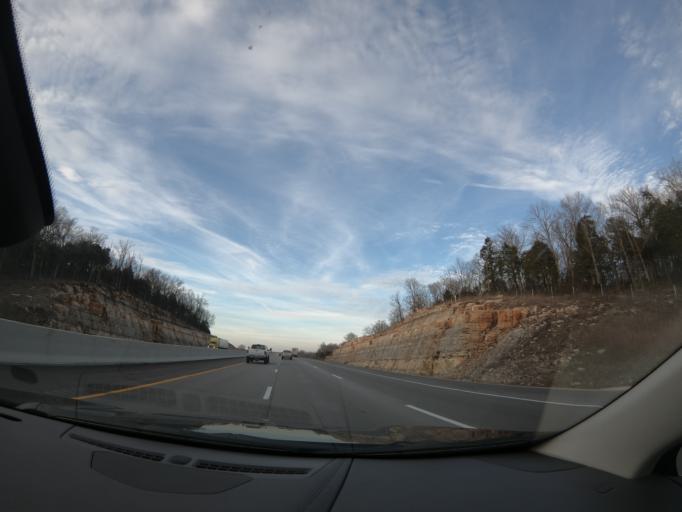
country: US
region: Kentucky
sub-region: Larue County
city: Hodgenville
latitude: 37.4696
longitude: -85.8819
